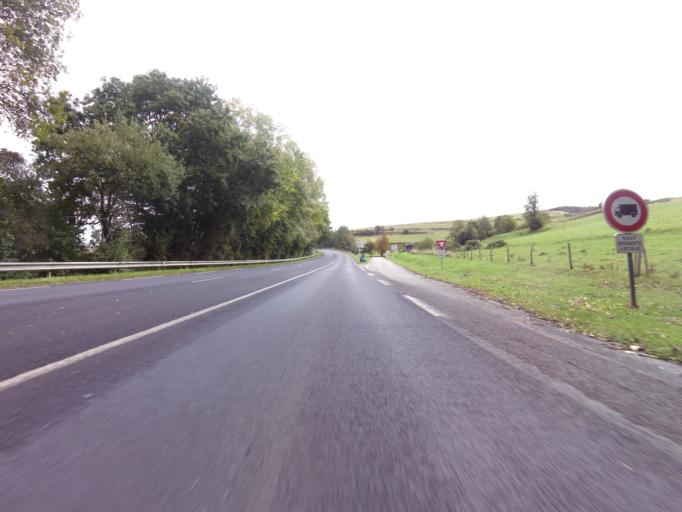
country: FR
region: Haute-Normandie
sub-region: Departement de la Seine-Maritime
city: Criel-sur-Mer
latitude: 50.0118
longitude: 1.3035
